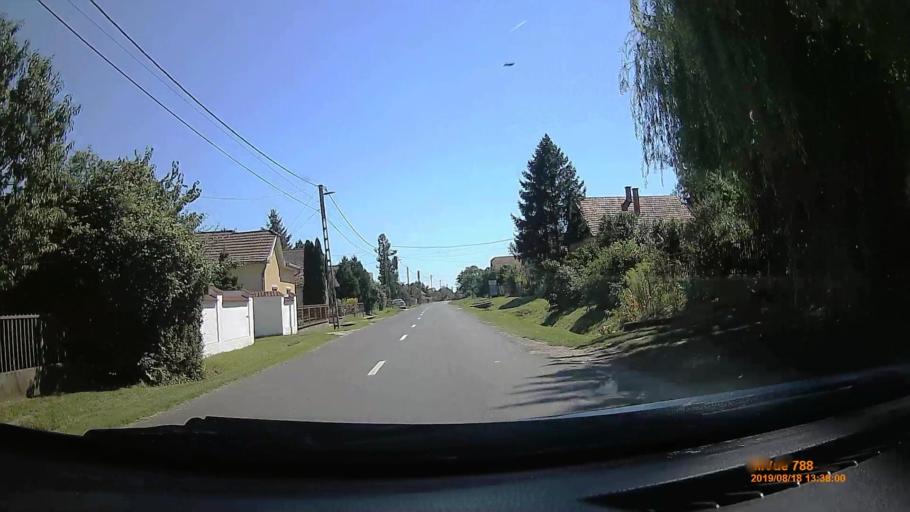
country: HU
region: Fejer
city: Cece
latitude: 46.7846
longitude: 18.5911
